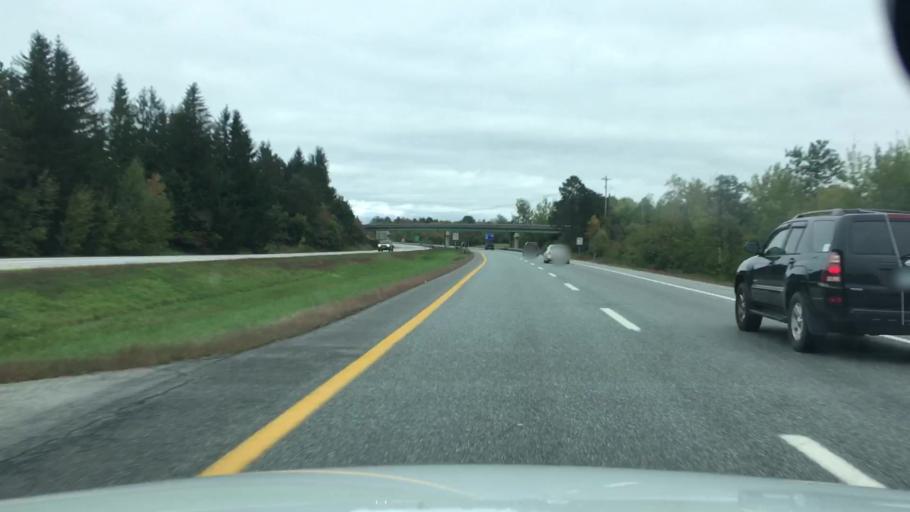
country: US
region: Maine
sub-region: Penobscot County
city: Hampden
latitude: 44.7800
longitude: -68.8206
